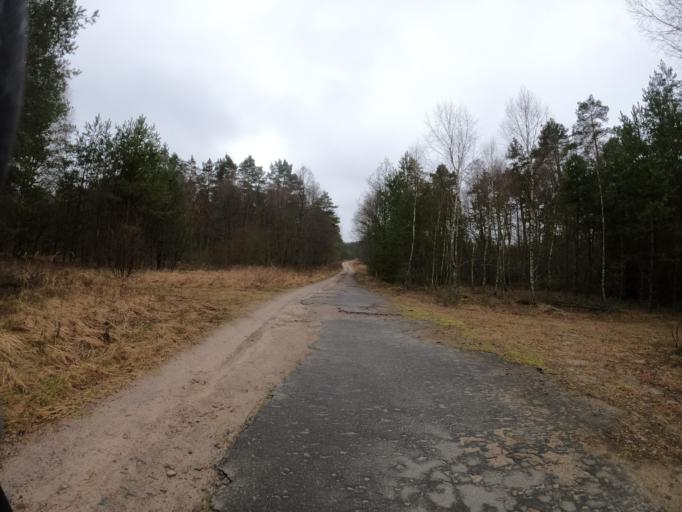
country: PL
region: Greater Poland Voivodeship
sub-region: Powiat zlotowski
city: Sypniewo
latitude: 53.5020
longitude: 16.5608
